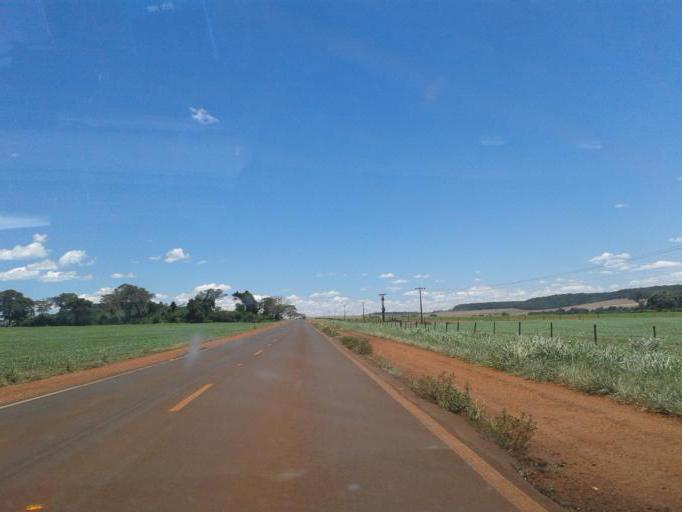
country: BR
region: Minas Gerais
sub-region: Capinopolis
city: Capinopolis
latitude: -18.6012
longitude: -49.5225
